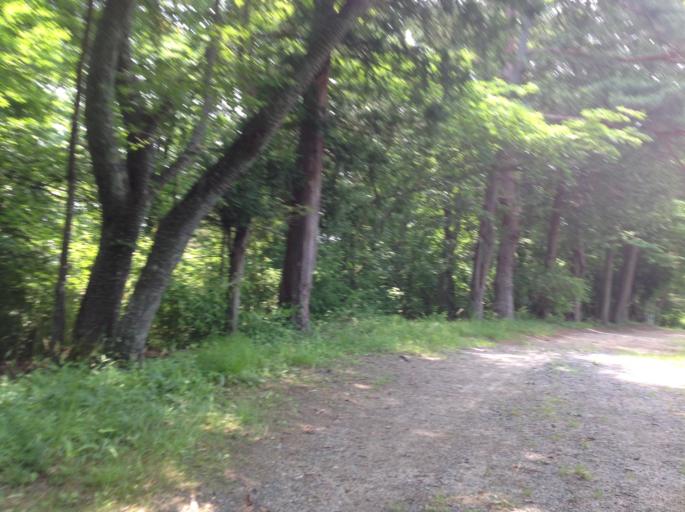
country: JP
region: Iwate
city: Ichinoseki
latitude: 38.9419
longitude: 141.1227
